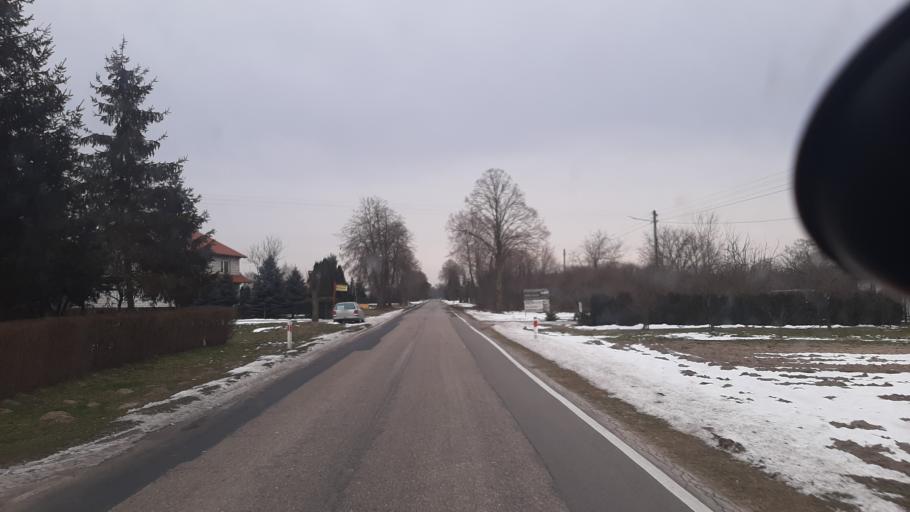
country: PL
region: Lublin Voivodeship
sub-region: Powiat lubartowski
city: Kamionka
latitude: 51.4597
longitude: 22.4206
